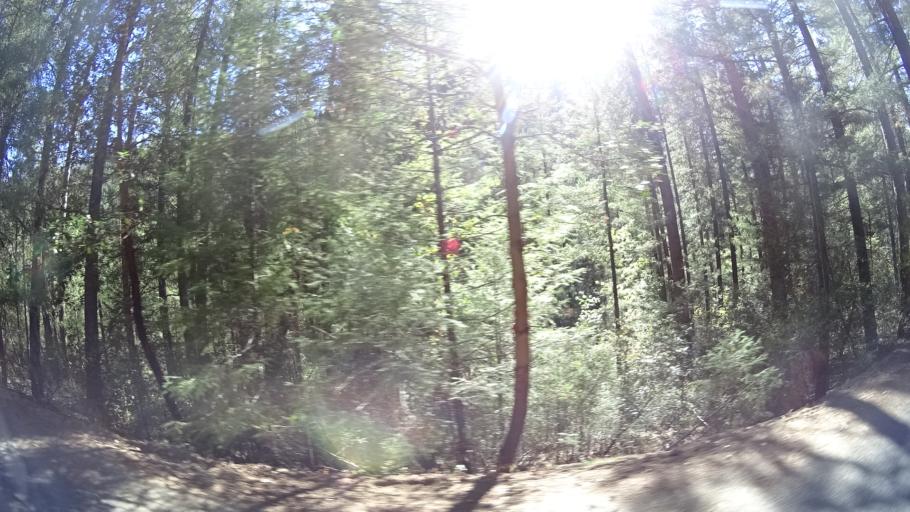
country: US
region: California
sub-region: Siskiyou County
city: Happy Camp
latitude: 41.3010
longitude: -123.1449
